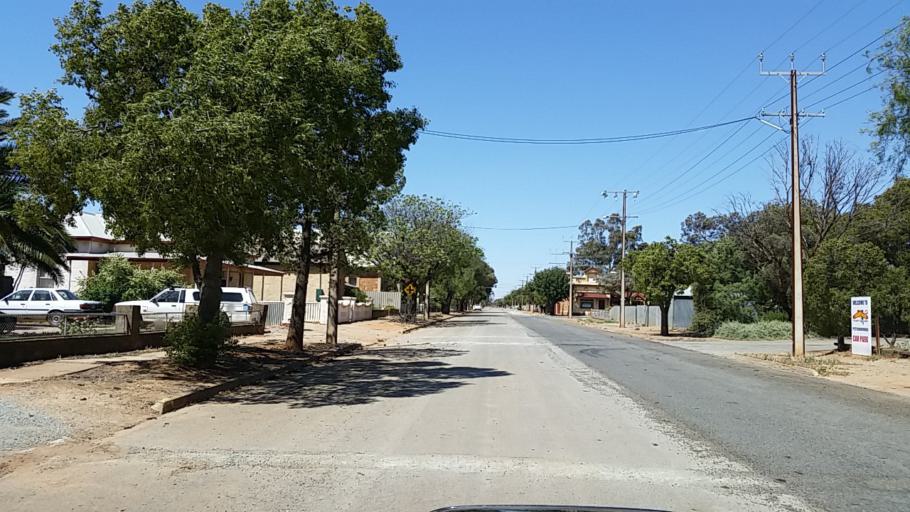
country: AU
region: South Australia
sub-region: Peterborough
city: Peterborough
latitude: -32.9723
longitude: 138.8367
